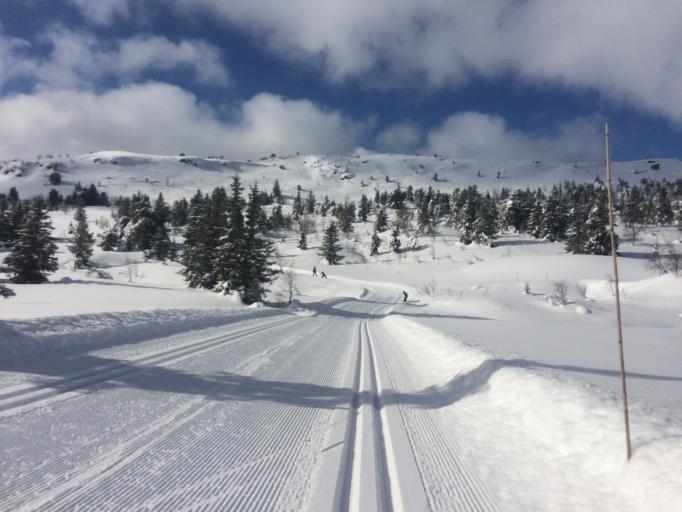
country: NO
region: Oppland
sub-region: Ringebu
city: Ringebu
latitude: 61.3557
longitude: 10.0559
